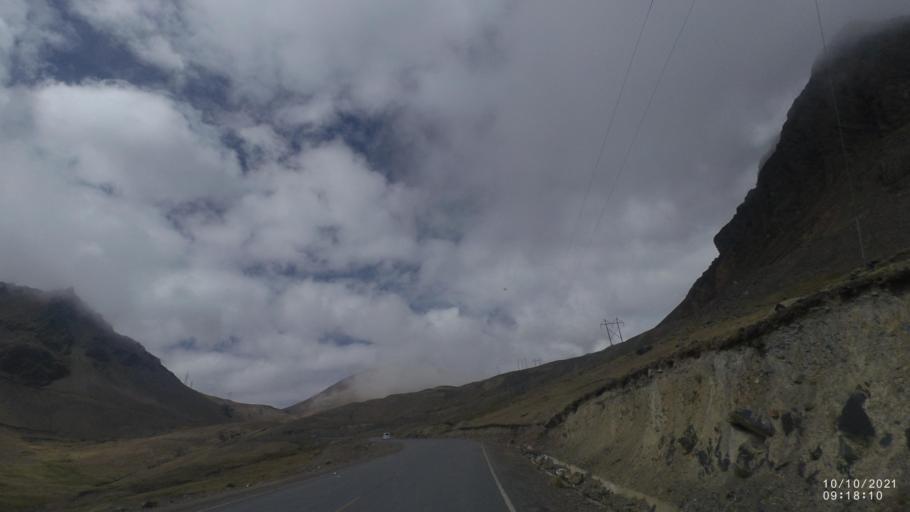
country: BO
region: La Paz
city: Quime
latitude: -17.0509
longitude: -67.2975
